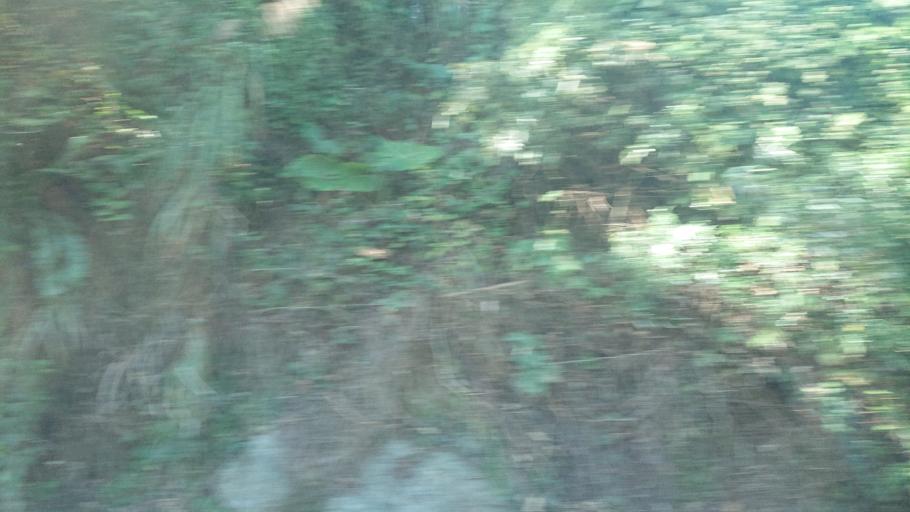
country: TW
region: Taiwan
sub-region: Chiayi
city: Jiayi Shi
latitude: 23.5362
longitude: 120.6354
